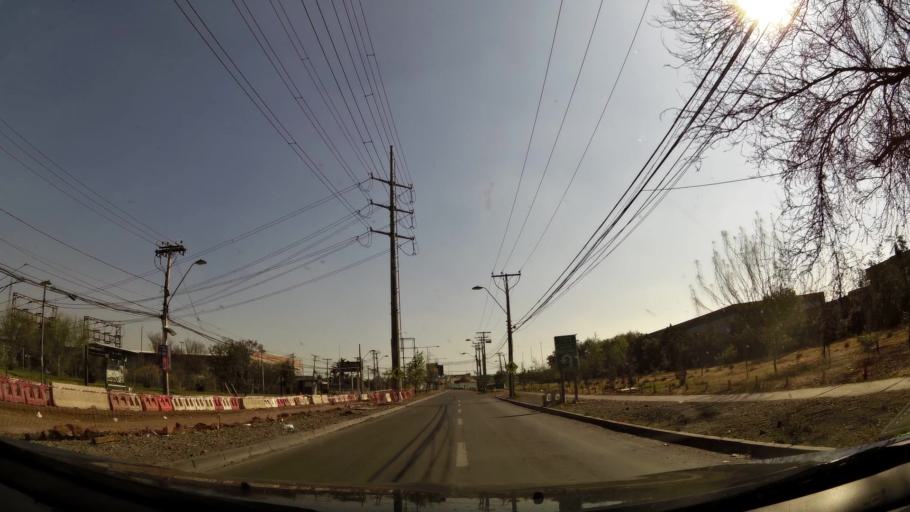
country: CL
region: Santiago Metropolitan
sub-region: Provincia de Chacabuco
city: Chicureo Abajo
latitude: -33.3329
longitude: -70.7113
